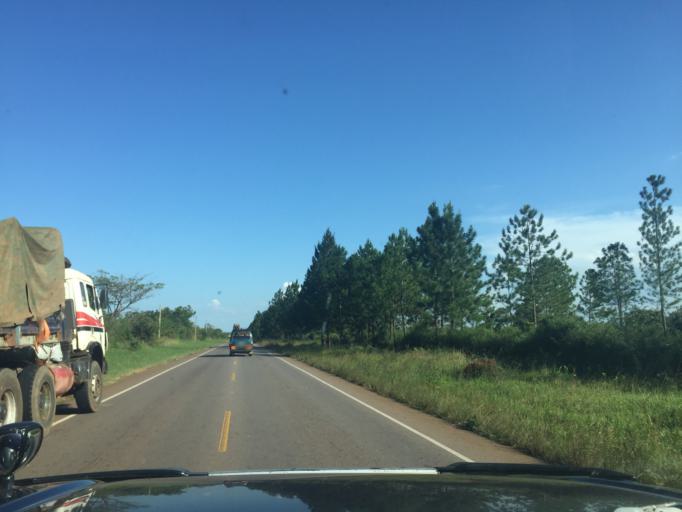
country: UG
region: Central Region
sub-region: Nakasongola District
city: Nakasongola
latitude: 1.3847
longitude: 32.3327
